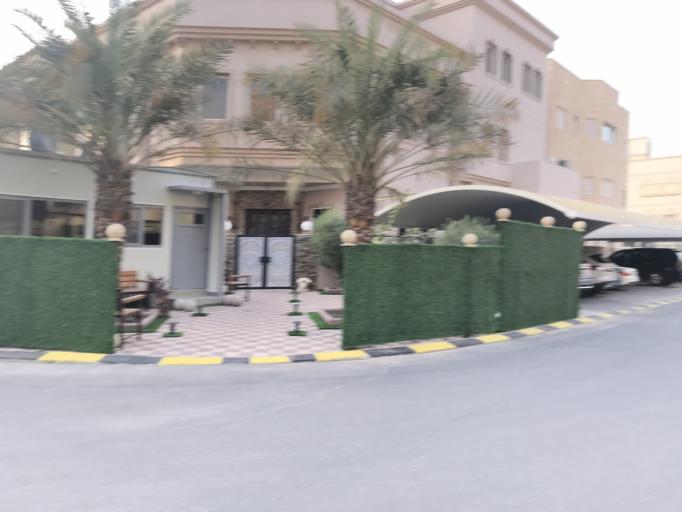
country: KW
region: Al Asimah
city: Ar Rabiyah
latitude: 29.2428
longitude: 47.9067
